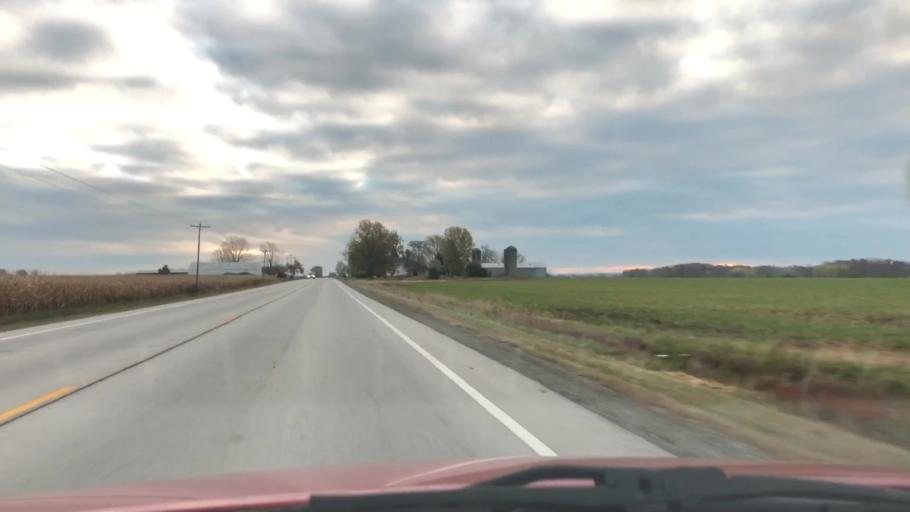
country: US
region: Wisconsin
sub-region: Brown County
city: Oneida
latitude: 44.4443
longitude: -88.1602
